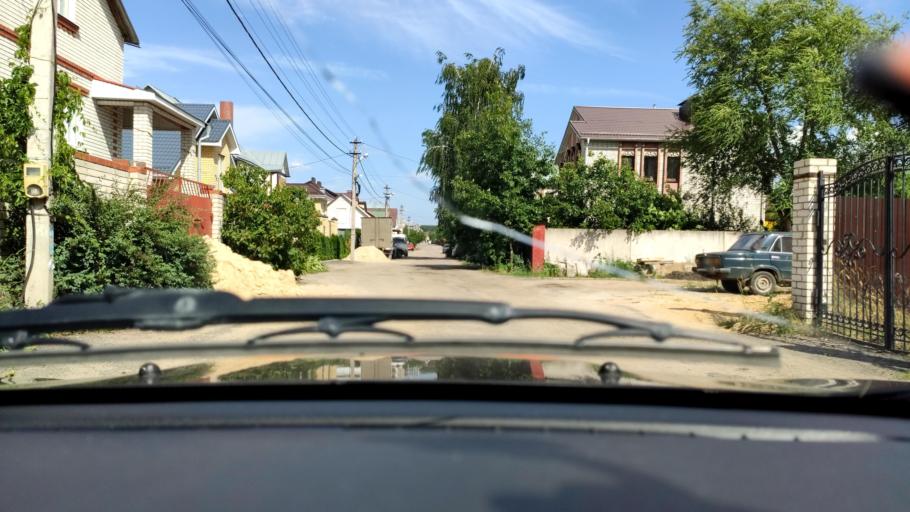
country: RU
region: Voronezj
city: Podgornoye
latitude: 51.7438
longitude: 39.1486
